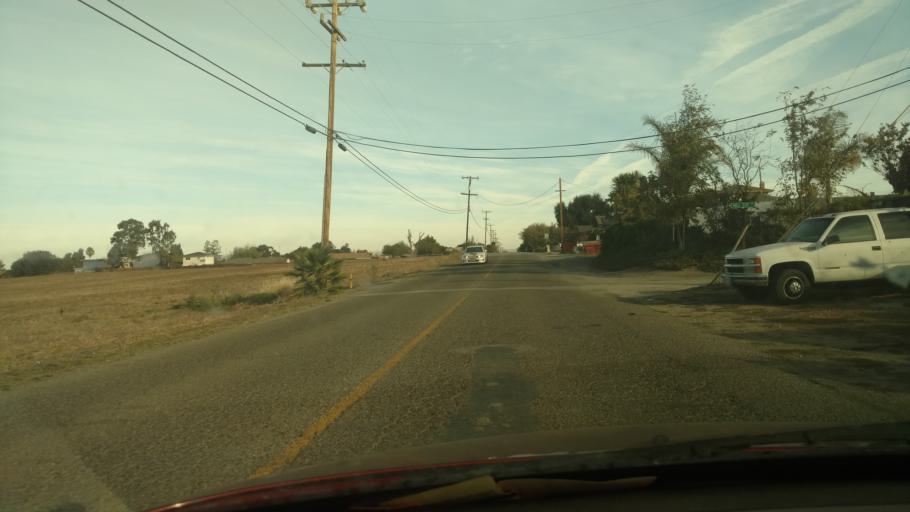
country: US
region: California
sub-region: San Benito County
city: Ridgemark
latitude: 36.8300
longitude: -121.3816
